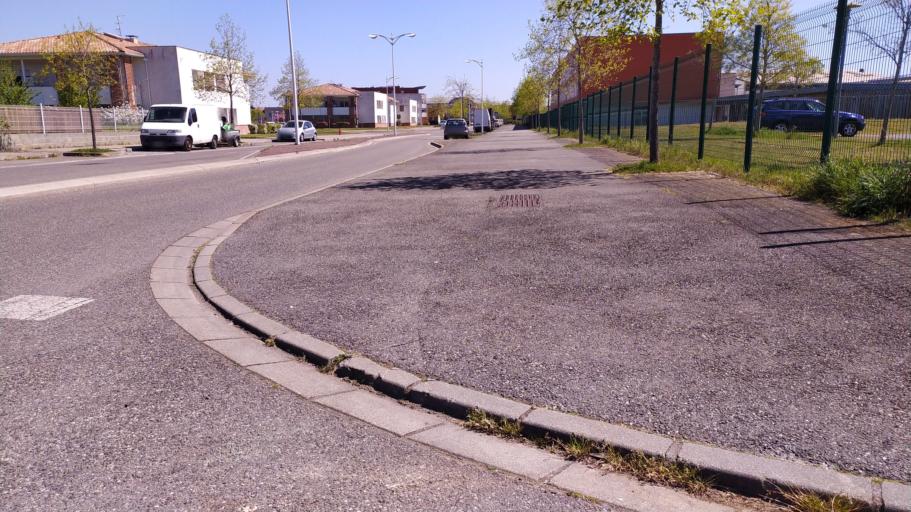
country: FR
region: Midi-Pyrenees
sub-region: Departement de la Haute-Garonne
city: Tournefeuille
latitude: 43.5784
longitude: 1.3111
